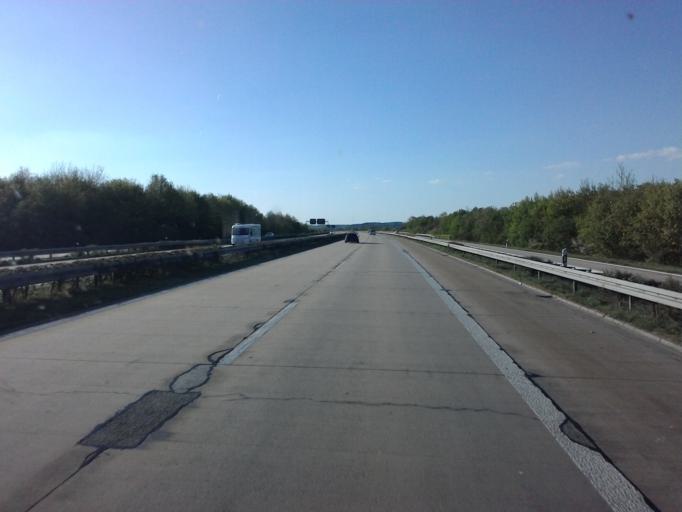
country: DE
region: Bavaria
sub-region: Regierungsbezirk Mittelfranken
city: Schnelldorf
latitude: 49.2039
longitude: 10.2335
